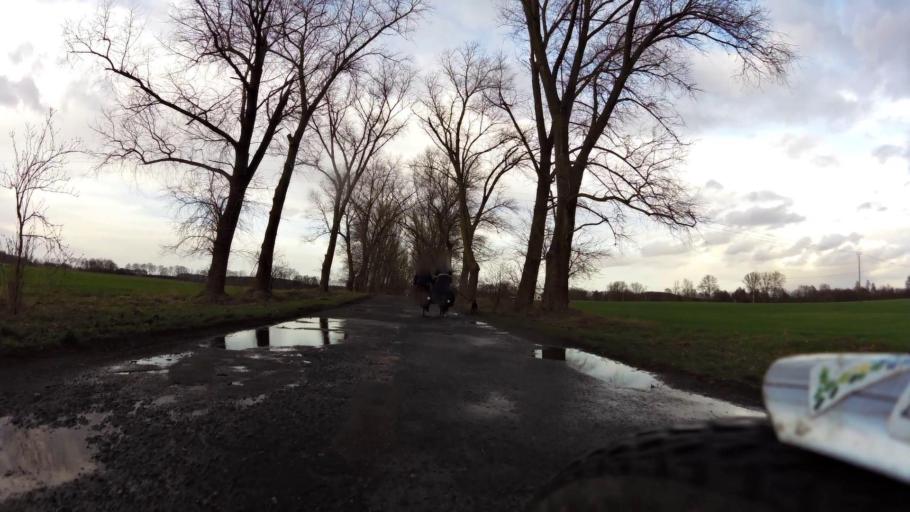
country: PL
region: West Pomeranian Voivodeship
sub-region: Powiat kamienski
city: Kamien Pomorski
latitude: 53.9135
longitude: 14.7313
